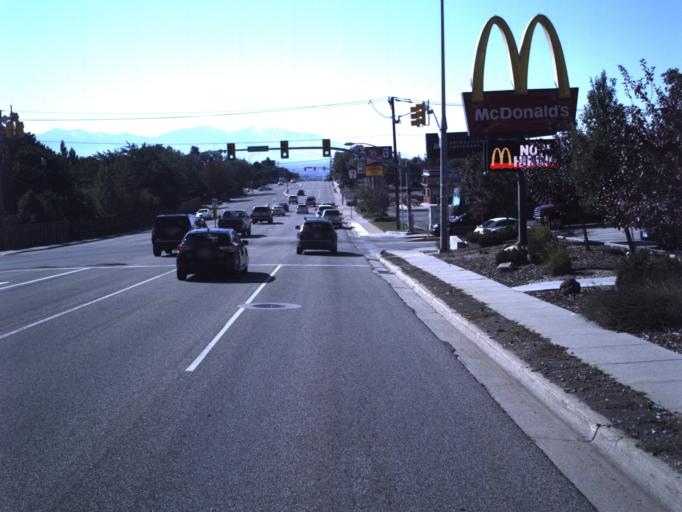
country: US
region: Utah
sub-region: Salt Lake County
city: East Millcreek
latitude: 40.7000
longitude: -111.8000
